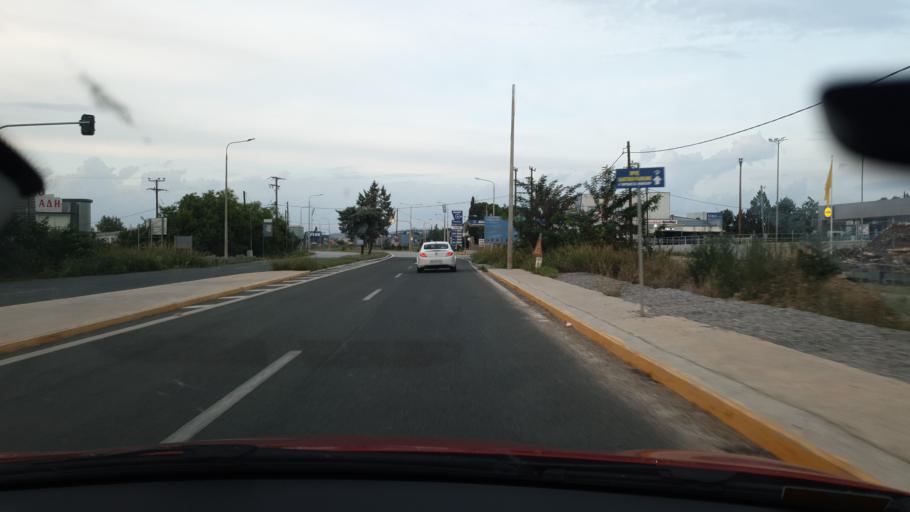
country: GR
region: Central Macedonia
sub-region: Nomos Kilkis
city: Kilkis
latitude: 40.9811
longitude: 22.8628
